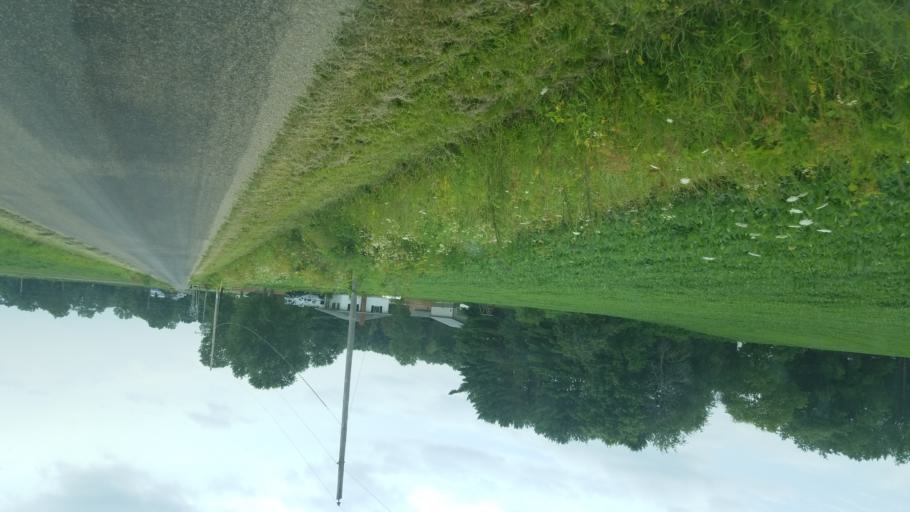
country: US
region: Ohio
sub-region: Knox County
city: Fredericktown
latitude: 40.4752
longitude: -82.5770
